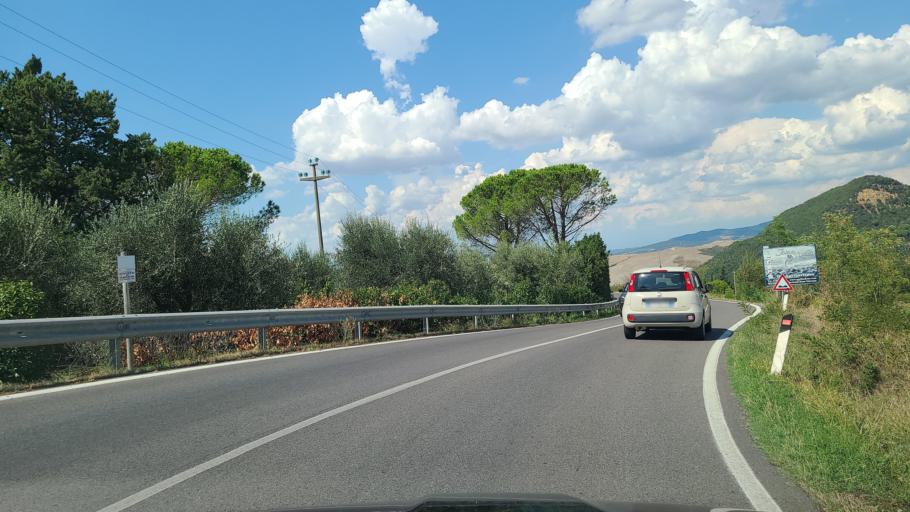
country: IT
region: Tuscany
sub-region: Province of Pisa
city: Volterra
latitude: 43.3865
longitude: 10.9031
